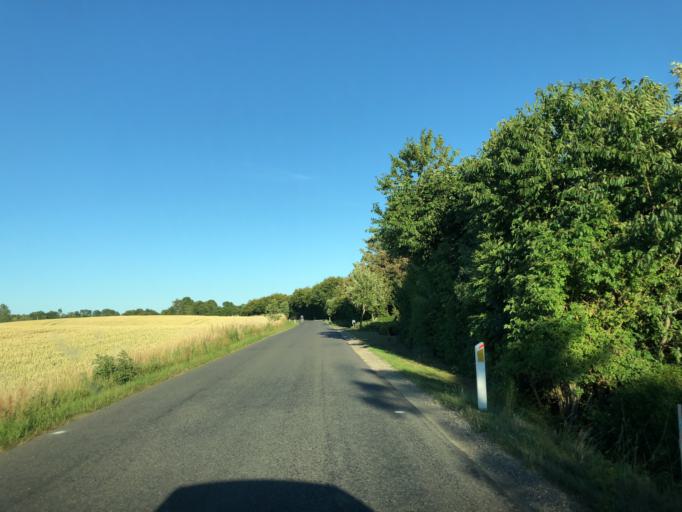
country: DK
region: Central Jutland
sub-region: Horsens Kommune
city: Horsens
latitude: 55.9452
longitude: 9.8576
